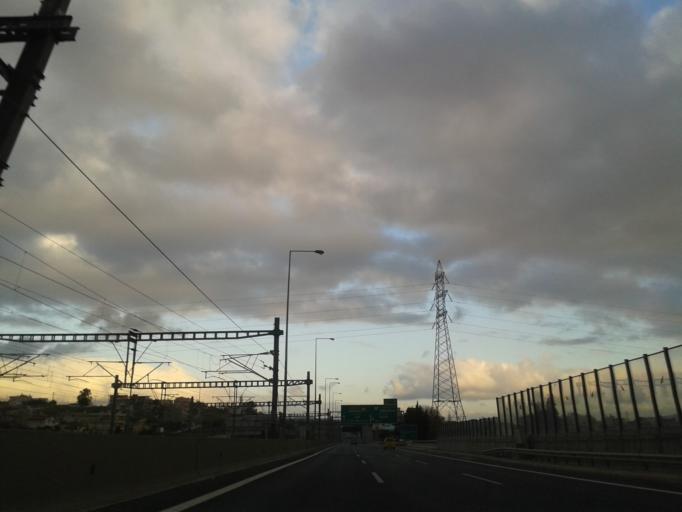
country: GR
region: Attica
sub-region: Nomarchia Dytikis Attikis
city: Zefyri
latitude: 38.0690
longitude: 23.7210
